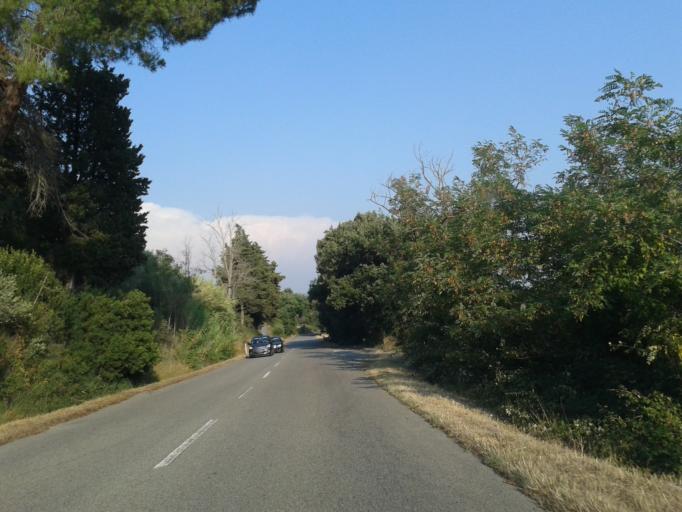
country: IT
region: Tuscany
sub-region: Provincia di Livorno
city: Rosignano Marittimo
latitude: 43.4010
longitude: 10.4806
